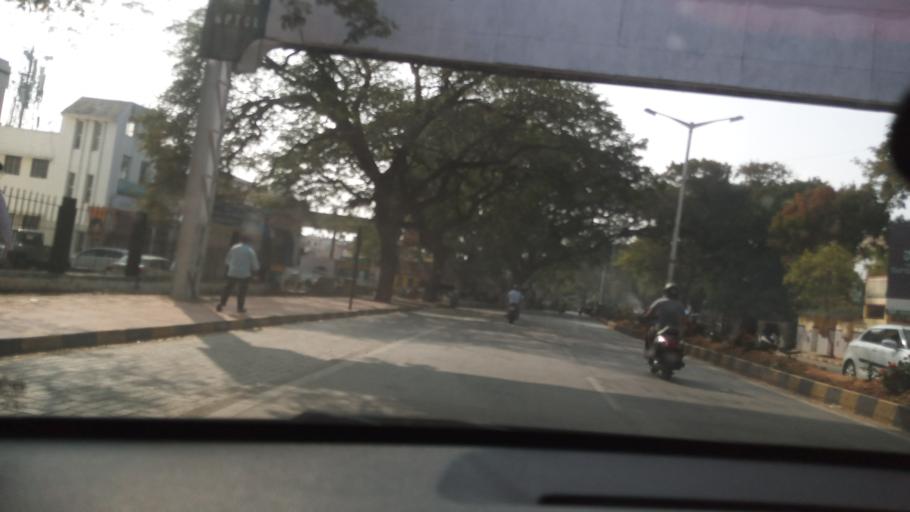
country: IN
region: Karnataka
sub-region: Mysore
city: Mysore
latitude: 12.3015
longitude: 76.6527
